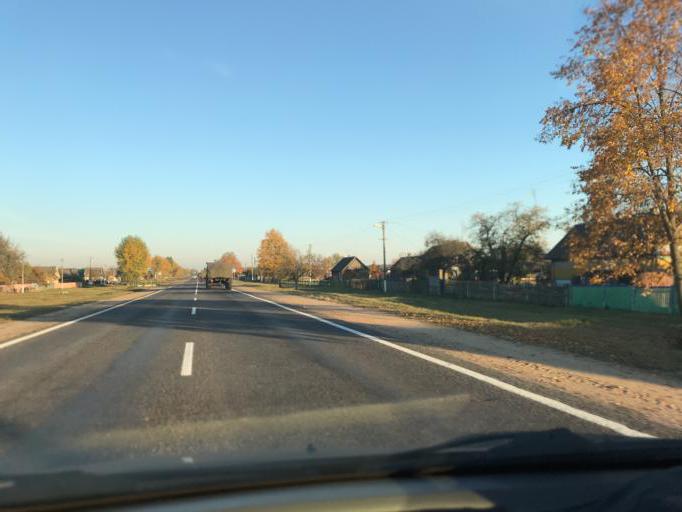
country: BY
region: Minsk
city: Staryya Darohi
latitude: 53.0462
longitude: 28.1068
